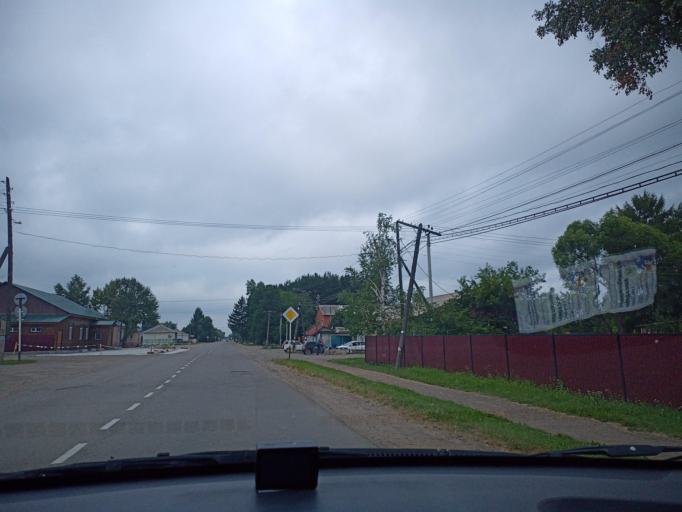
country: RU
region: Primorskiy
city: Novopokrovka
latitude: 45.8983
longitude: 134.8862
